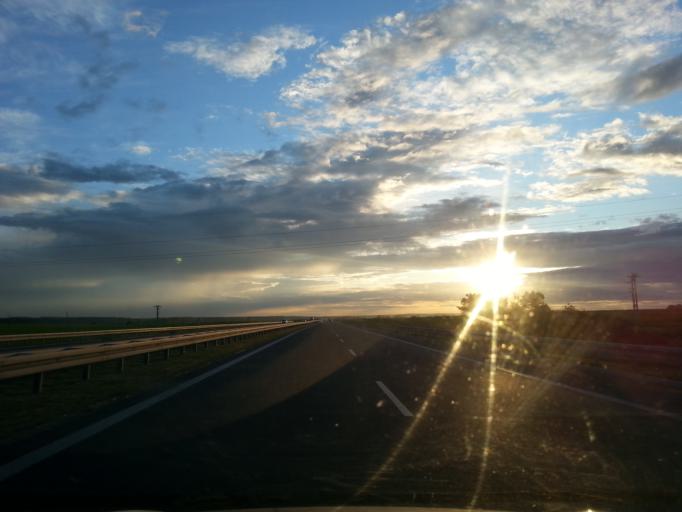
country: PL
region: Lower Silesian Voivodeship
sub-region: Powiat olesnicki
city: Sycow
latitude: 51.2968
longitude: 17.6659
